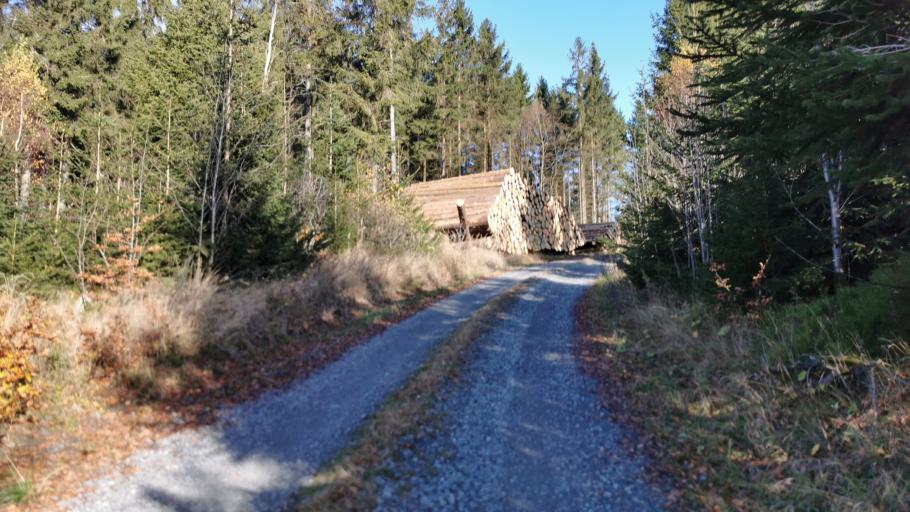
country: DE
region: Bavaria
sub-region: Upper Franconia
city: Reichenbach
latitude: 50.4260
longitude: 11.4323
